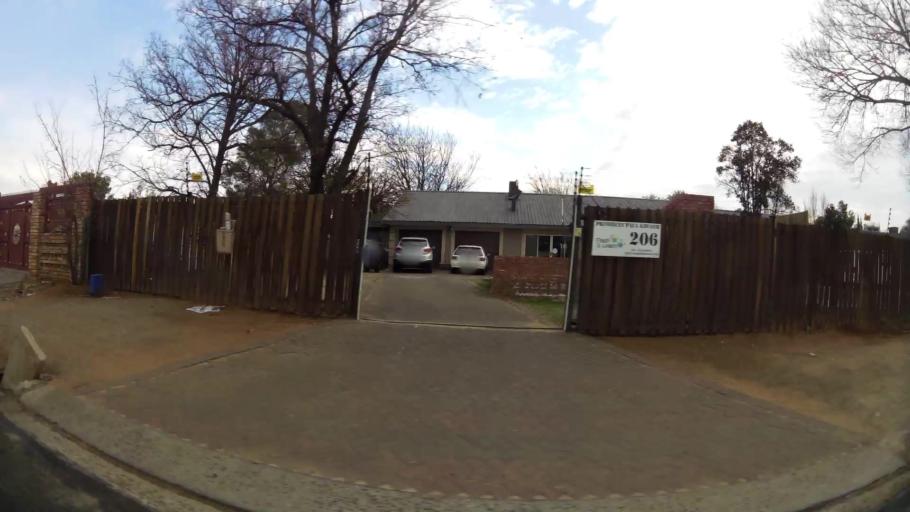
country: ZA
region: Orange Free State
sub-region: Mangaung Metropolitan Municipality
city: Bloemfontein
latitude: -29.1188
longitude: 26.1775
